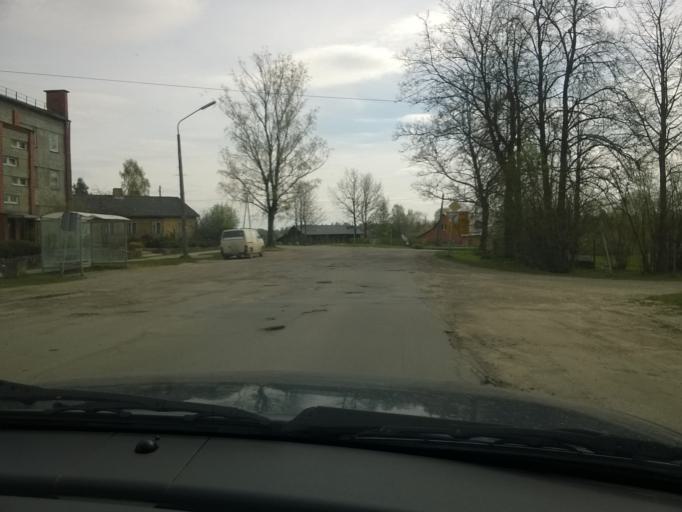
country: LV
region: Vilanu
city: Vilani
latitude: 56.5423
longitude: 26.9267
